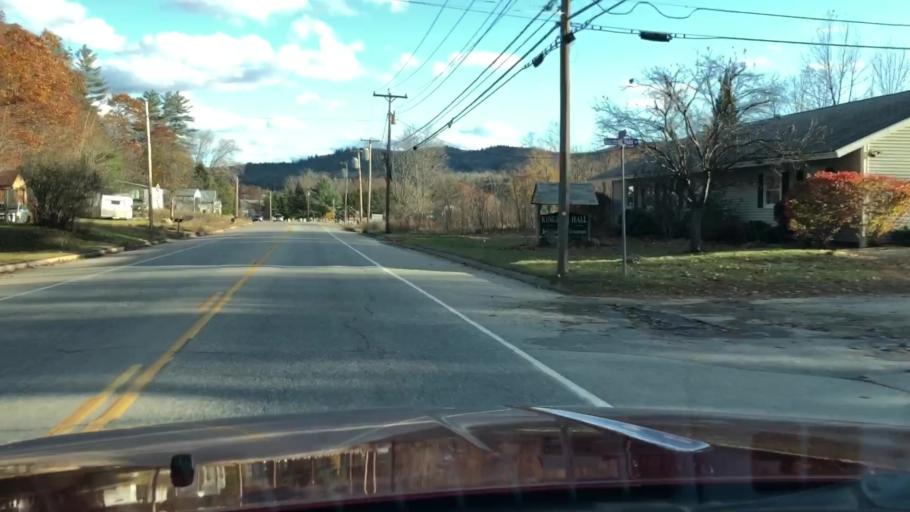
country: US
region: Maine
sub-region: Oxford County
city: Mexico
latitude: 44.5382
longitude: -70.5144
